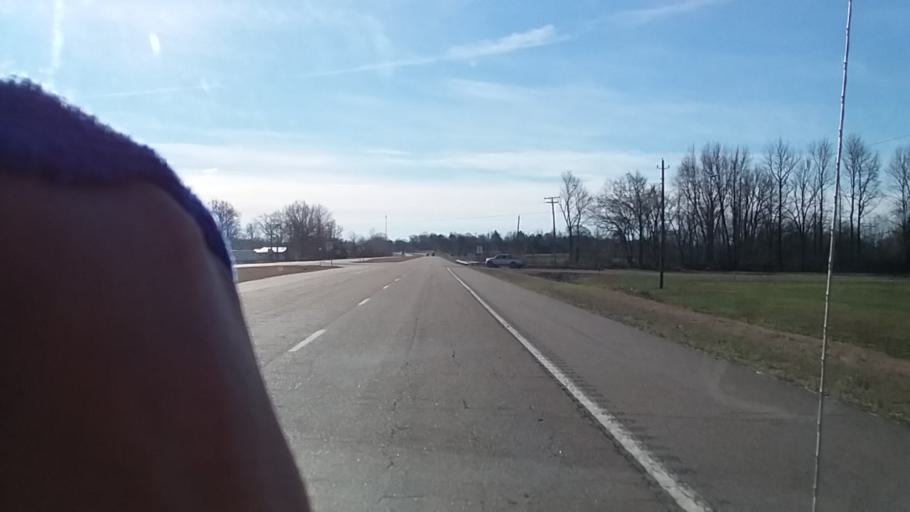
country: US
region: Tennessee
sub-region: Lauderdale County
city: Halls
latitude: 35.9236
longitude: -89.2795
